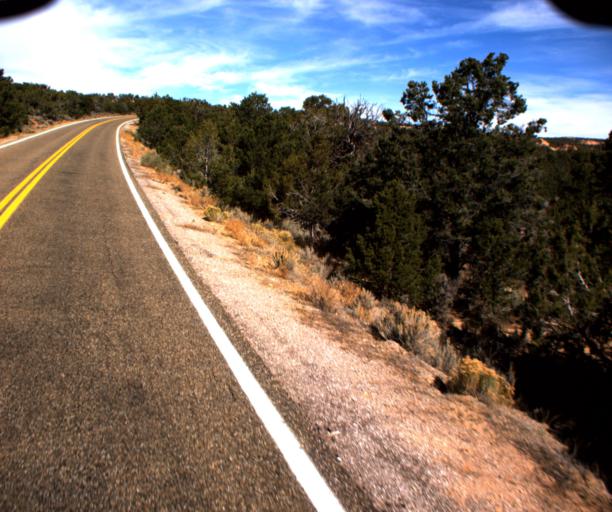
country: US
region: Arizona
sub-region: Navajo County
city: Kayenta
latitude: 36.6215
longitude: -110.5082
